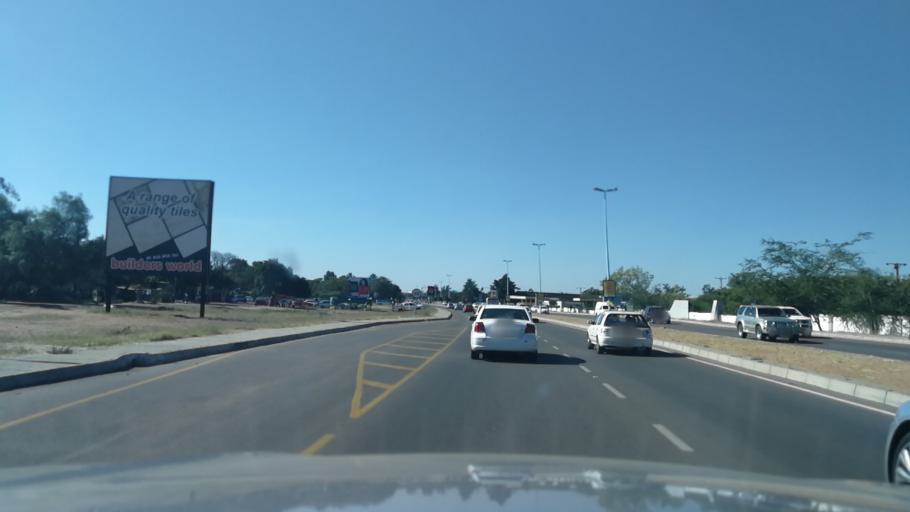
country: BW
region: South East
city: Gaborone
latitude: -24.6791
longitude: 25.9177
